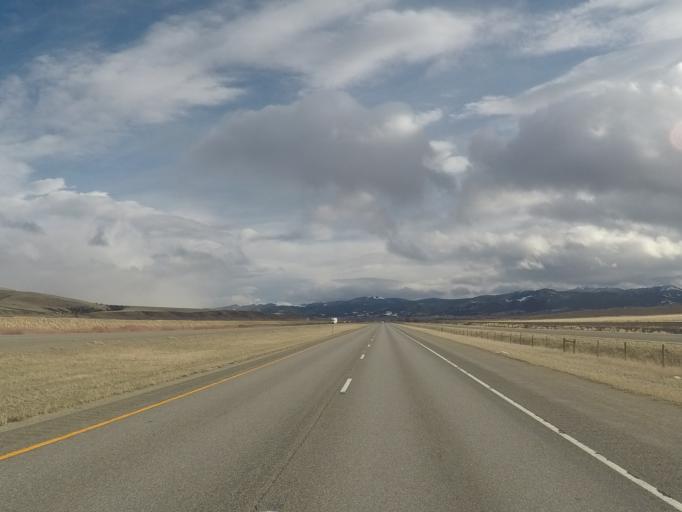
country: US
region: Montana
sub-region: Deer Lodge County
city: Warm Springs
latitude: 46.1501
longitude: -112.7936
